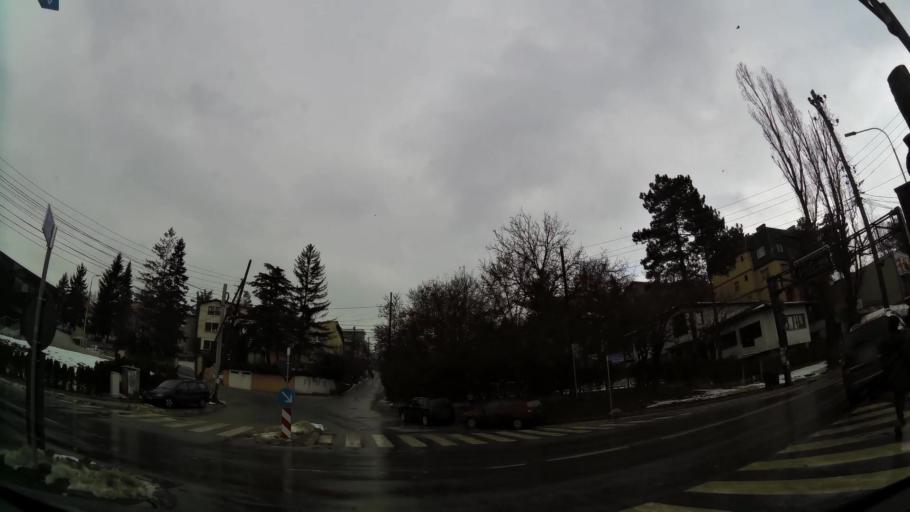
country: XK
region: Pristina
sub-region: Komuna e Prishtines
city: Pristina
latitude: 42.6662
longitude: 21.1776
